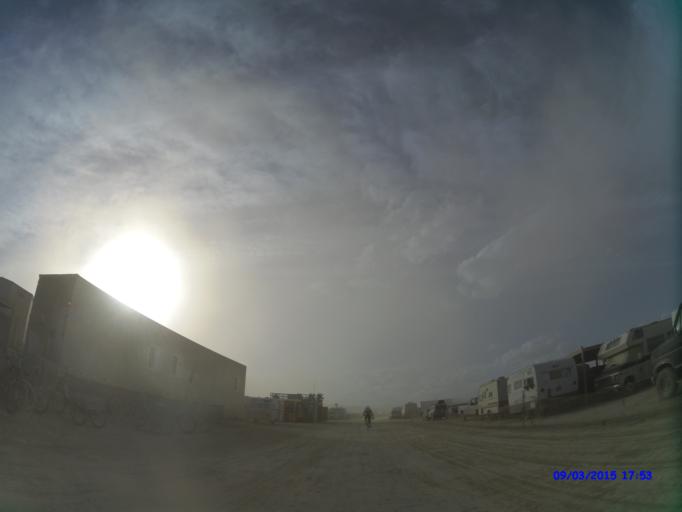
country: US
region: Nevada
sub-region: Pershing County
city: Lovelock
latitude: 40.7778
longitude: -119.2149
